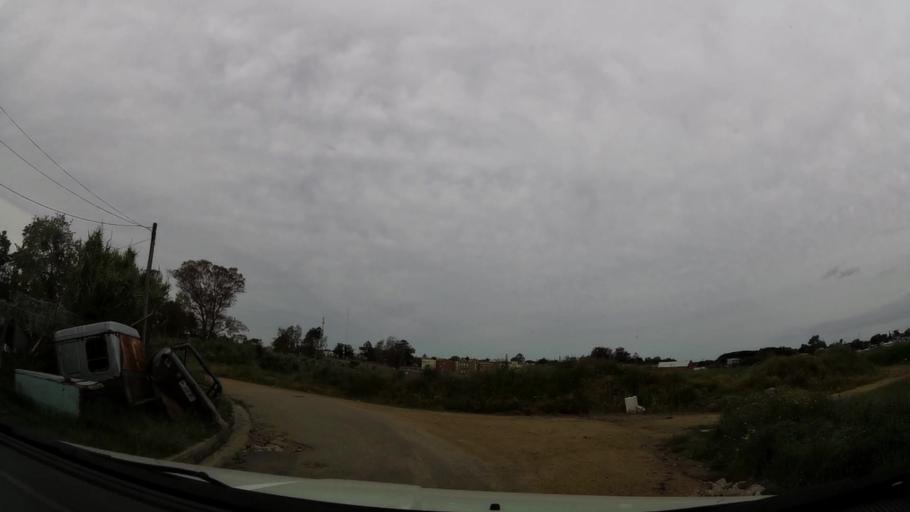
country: UY
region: Maldonado
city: Maldonado
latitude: -34.8775
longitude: -54.9768
